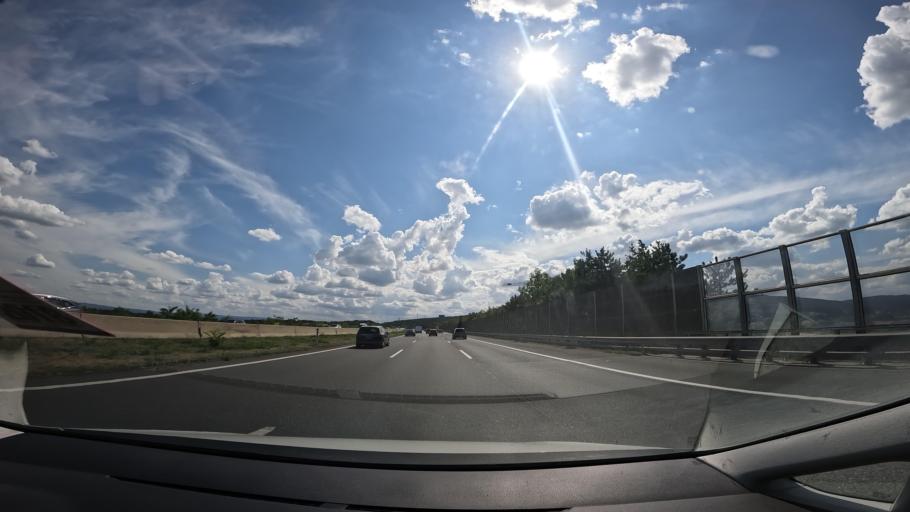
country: AT
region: Lower Austria
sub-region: Politischer Bezirk Wiener Neustadt
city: Theresienfeld
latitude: 47.8621
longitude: 16.1892
